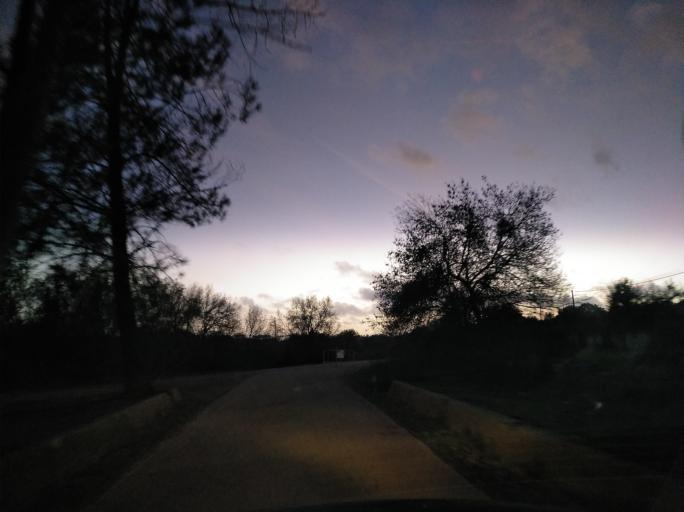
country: PT
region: Portalegre
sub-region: Campo Maior
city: Campo Maior
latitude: 39.0798
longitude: -7.0188
